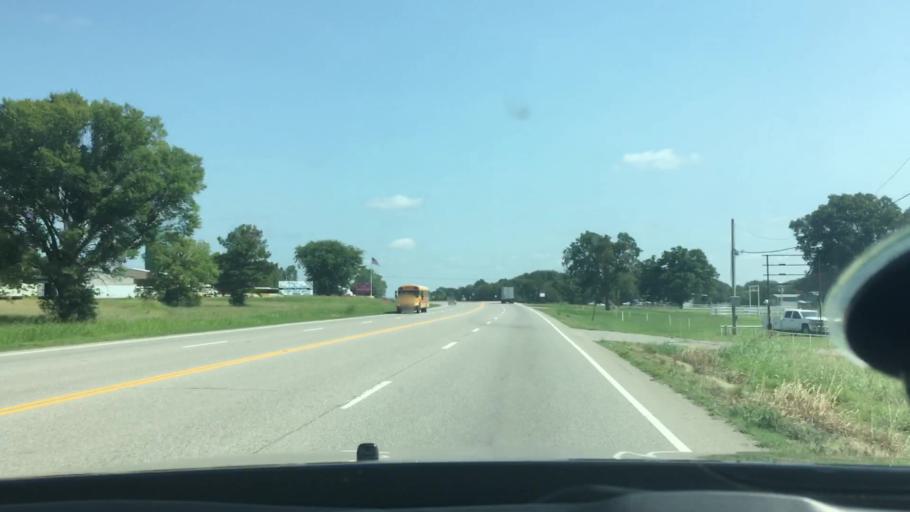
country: US
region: Oklahoma
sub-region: Atoka County
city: Atoka
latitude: 34.3424
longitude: -96.1531
